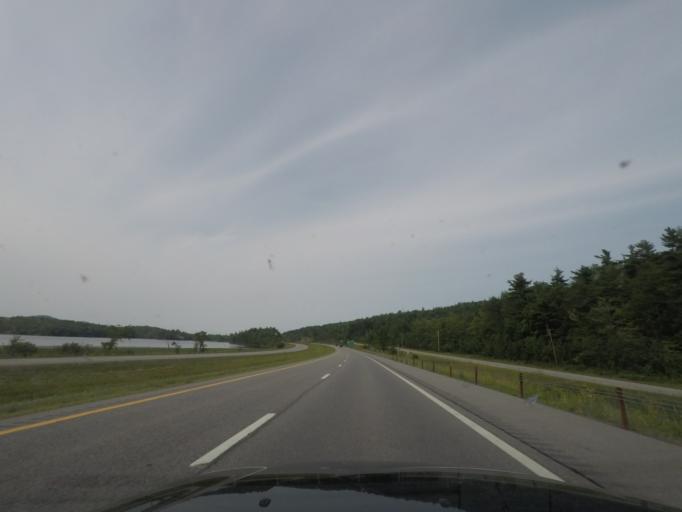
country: US
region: New York
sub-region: Essex County
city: Keeseville
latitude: 44.4230
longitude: -73.4936
